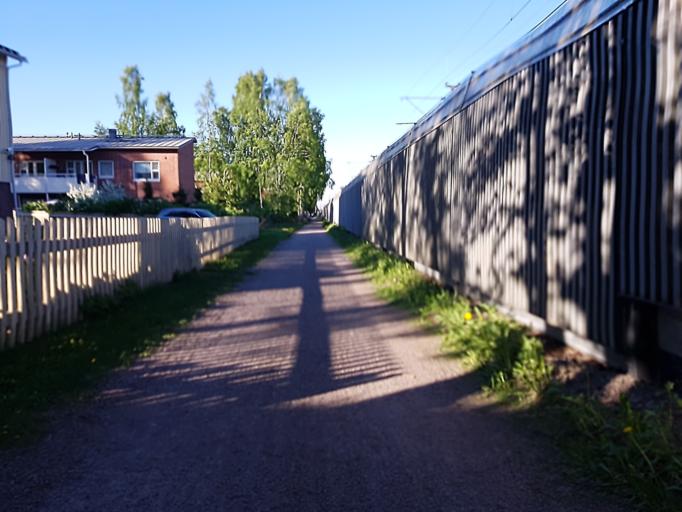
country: FI
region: Uusimaa
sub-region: Helsinki
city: Helsinki
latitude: 60.2264
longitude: 24.9622
